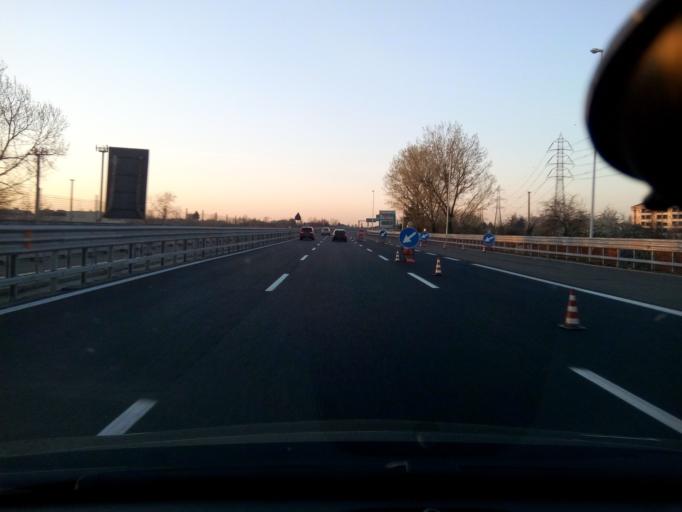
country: IT
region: Lombardy
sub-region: Citta metropolitana di Milano
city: Rho
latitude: 45.5361
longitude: 9.0591
